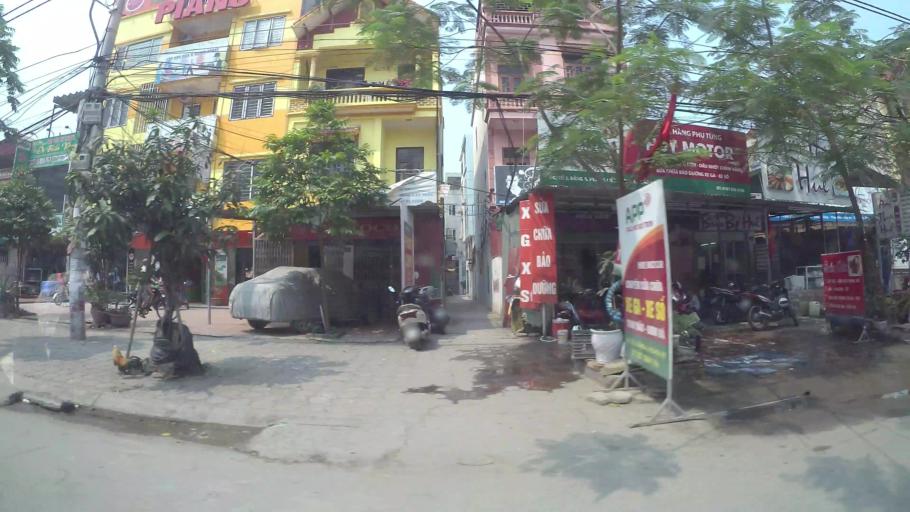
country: VN
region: Ha Noi
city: Van Dien
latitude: 20.9637
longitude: 105.8215
